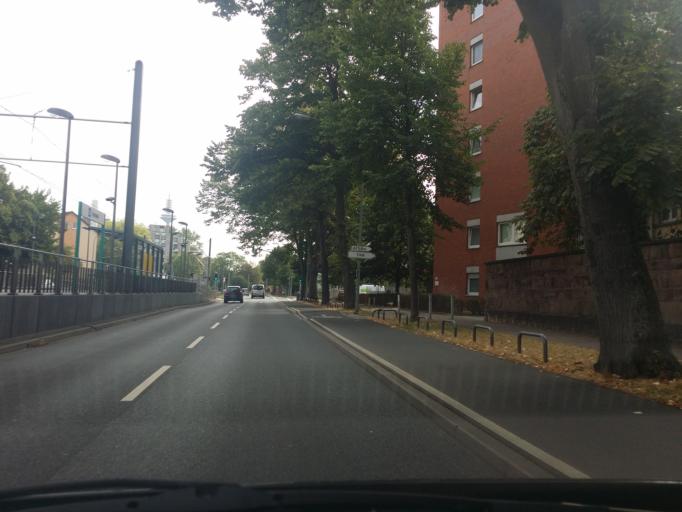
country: DE
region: Hesse
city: Niederrad
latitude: 50.1294
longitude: 8.6252
